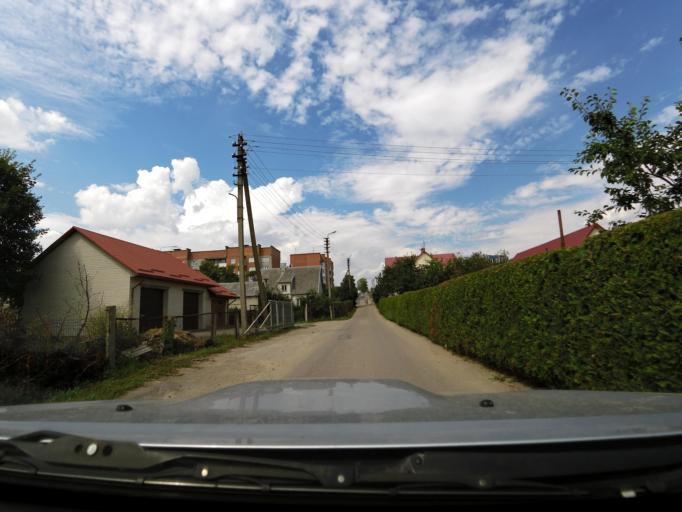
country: LT
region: Taurages apskritis
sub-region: Jurbarkas
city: Jurbarkas
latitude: 55.0787
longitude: 22.7815
